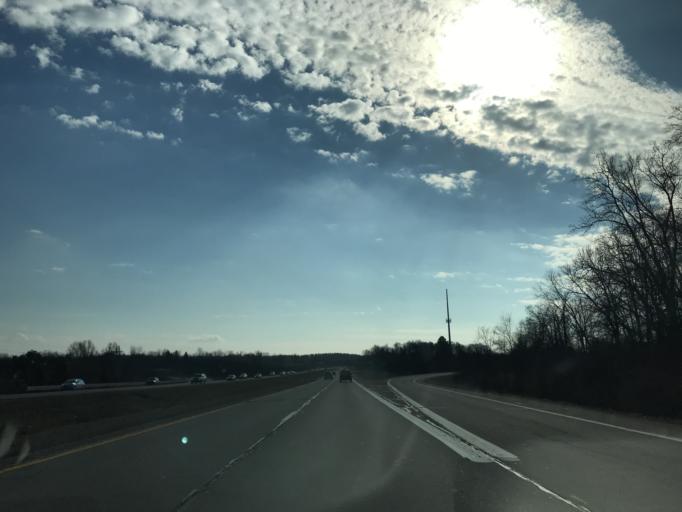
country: US
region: Michigan
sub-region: Washtenaw County
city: Ann Arbor
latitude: 42.2792
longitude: -83.6764
